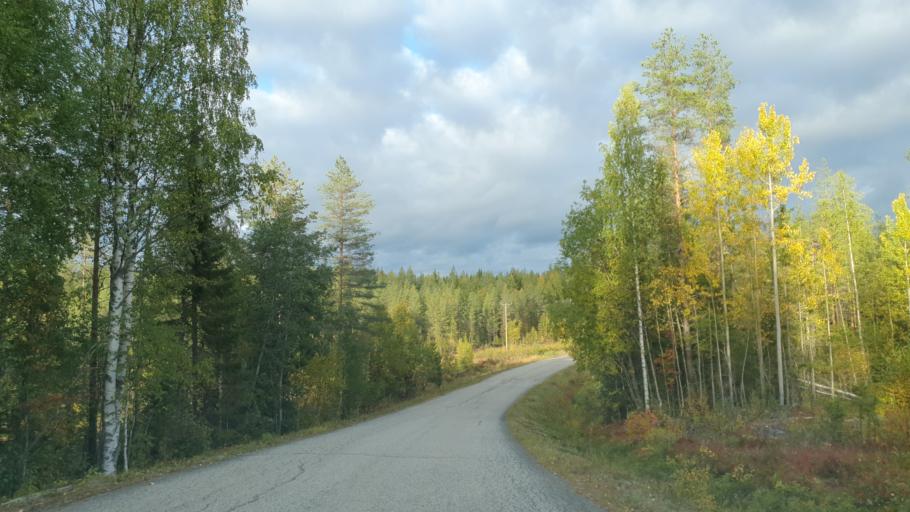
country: FI
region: North Karelia
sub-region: Pielisen Karjala
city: Lieksa
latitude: 63.9198
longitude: 30.1325
